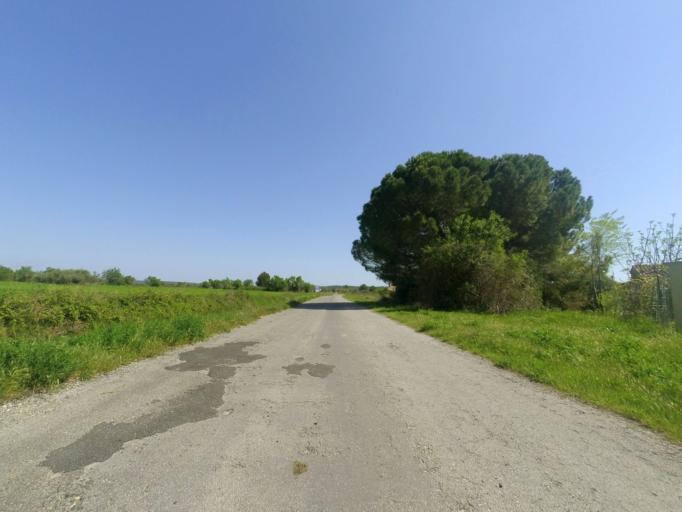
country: FR
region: Languedoc-Roussillon
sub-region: Departement du Gard
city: Congenies
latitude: 43.7765
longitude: 4.1656
